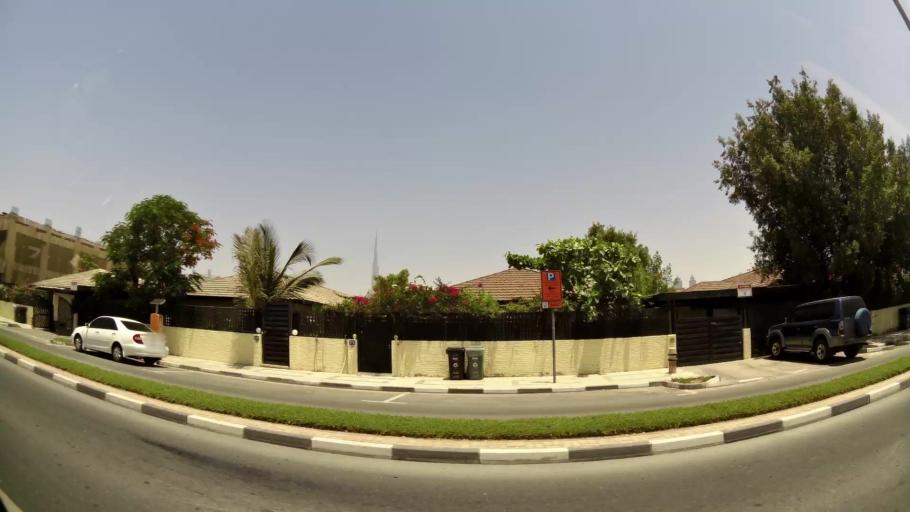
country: AE
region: Dubai
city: Dubai
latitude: 25.2063
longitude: 55.2440
